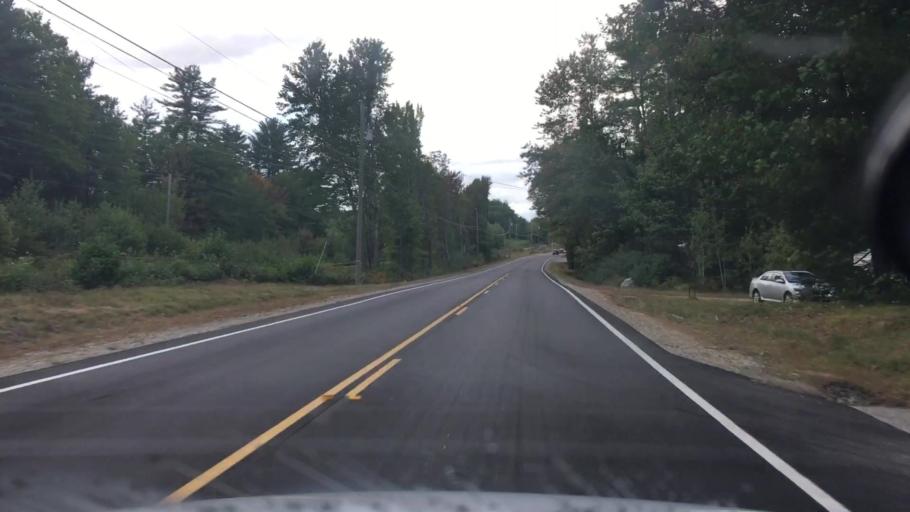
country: US
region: New Hampshire
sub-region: Carroll County
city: Sanbornville
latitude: 43.5392
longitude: -71.0270
